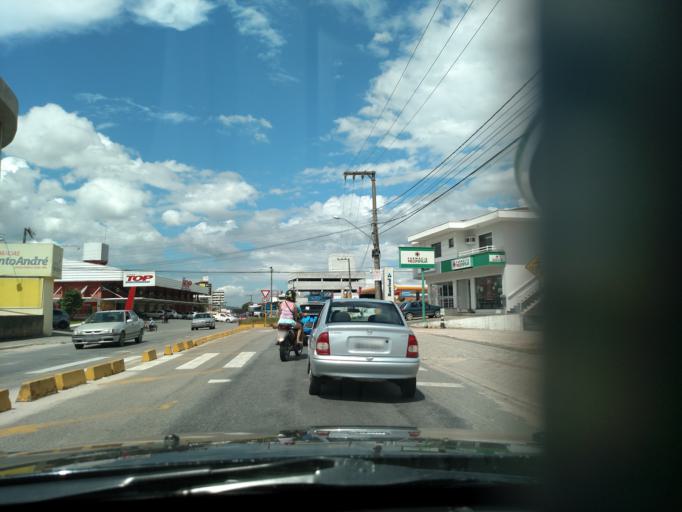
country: BR
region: Santa Catarina
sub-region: Gaspar
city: Gaspar
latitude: -26.9307
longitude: -48.9507
